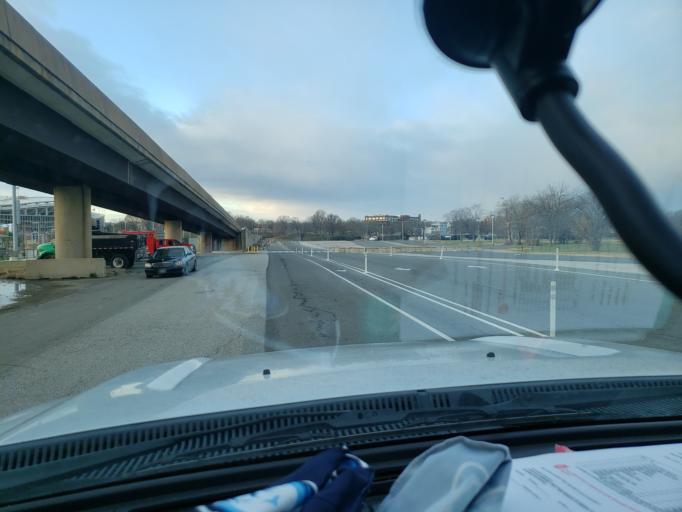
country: US
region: Maryland
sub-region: Prince George's County
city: Colmar Manor
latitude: 38.8954
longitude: -76.9697
